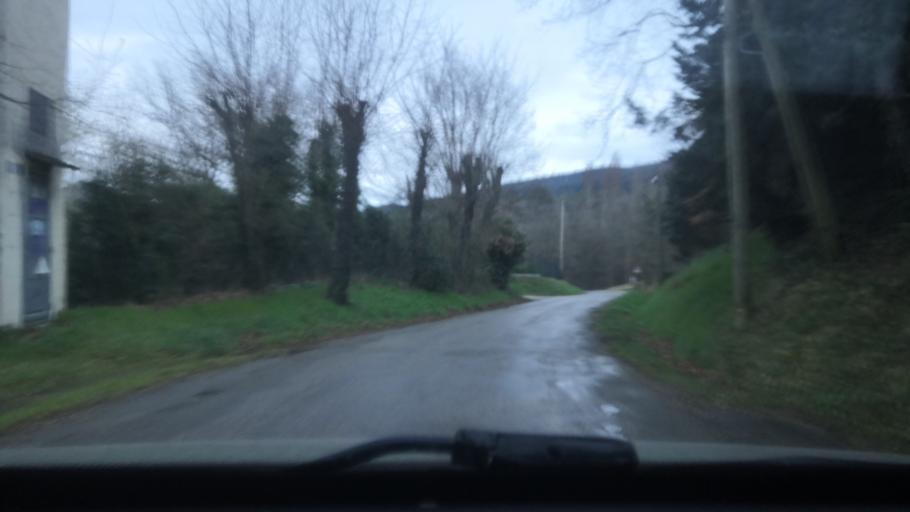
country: FR
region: Rhone-Alpes
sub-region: Departement de la Drome
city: Dieulefit
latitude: 44.5166
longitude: 5.0405
